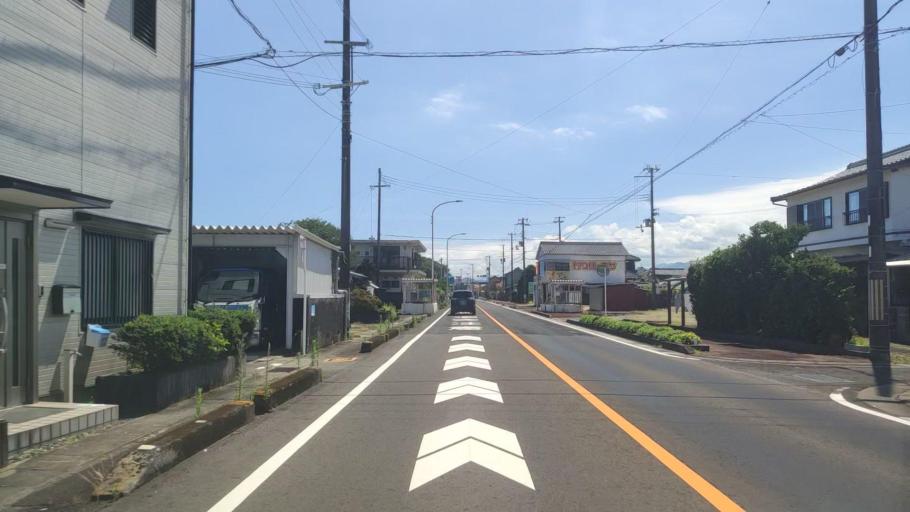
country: JP
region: Wakayama
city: Shingu
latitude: 33.8733
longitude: 136.0867
